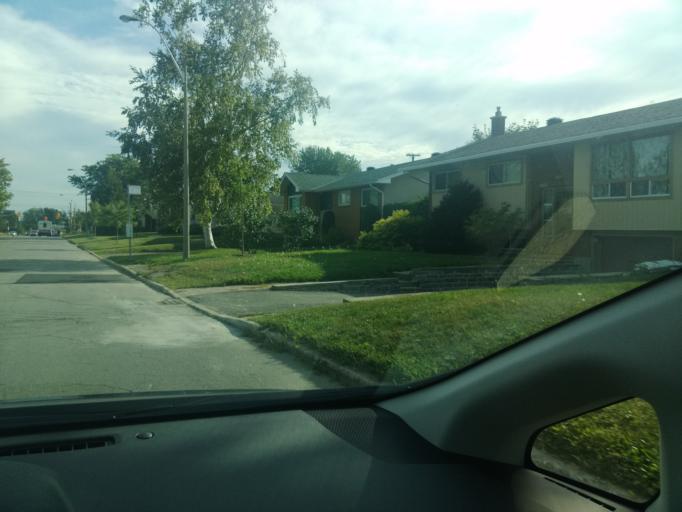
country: CA
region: Ontario
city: Ottawa
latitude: 45.3817
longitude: -75.6447
